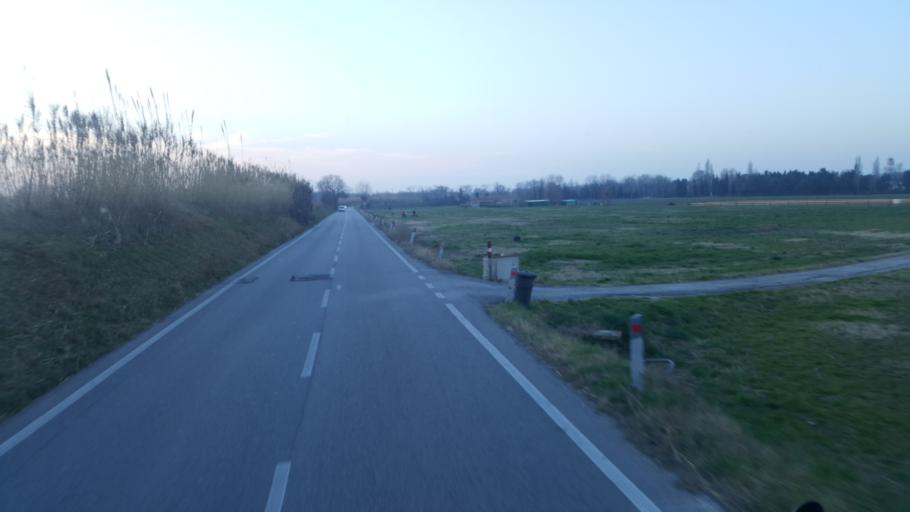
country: IT
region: The Marches
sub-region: Provincia di Ancona
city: Falconara Marittima
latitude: 43.6270
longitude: 13.3772
